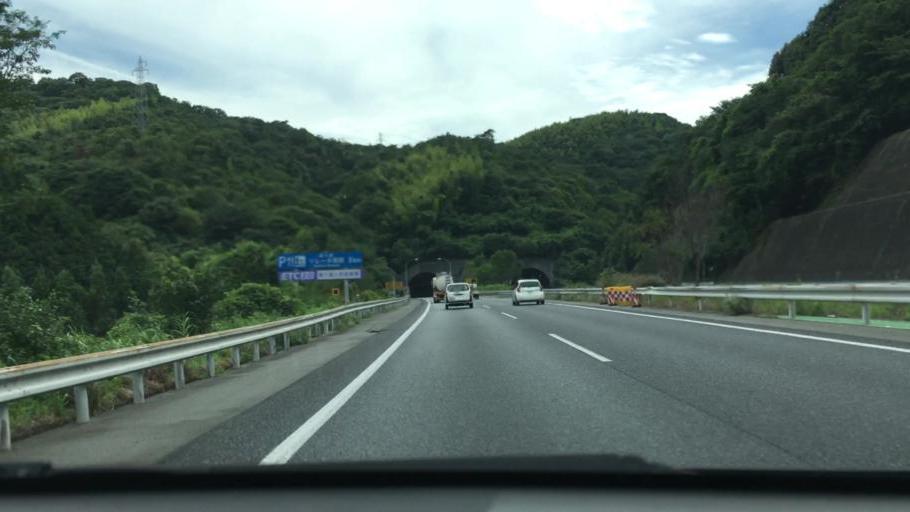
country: JP
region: Yamaguchi
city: Tokuyama
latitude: 34.0767
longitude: 131.7175
